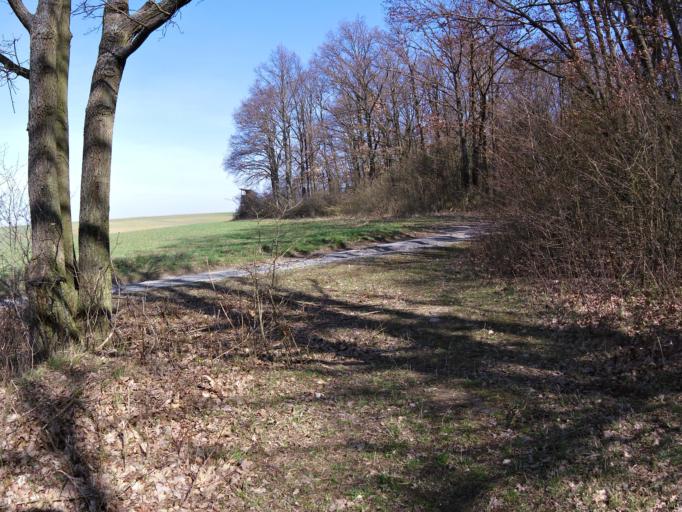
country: DE
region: Bavaria
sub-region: Regierungsbezirk Unterfranken
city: Rottendorf
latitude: 49.8106
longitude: 10.0169
